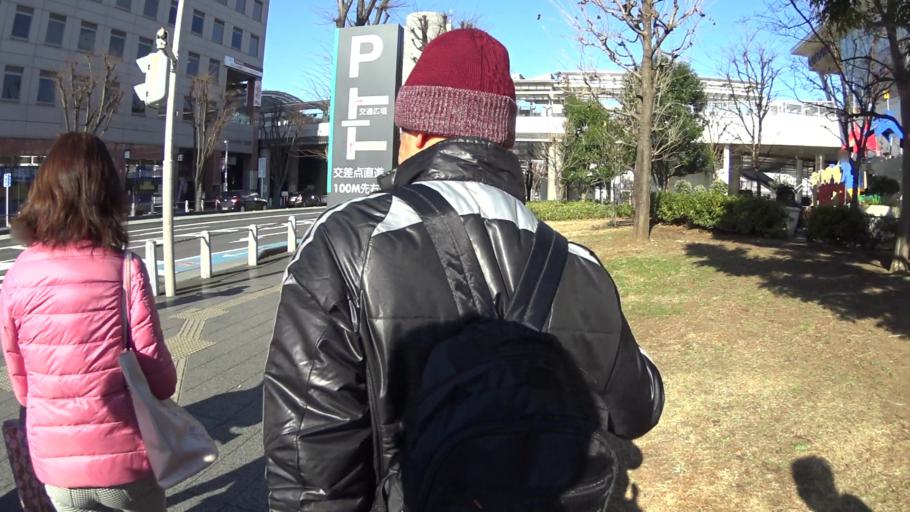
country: JP
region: Saitama
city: Yono
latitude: 35.9005
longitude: 139.6317
